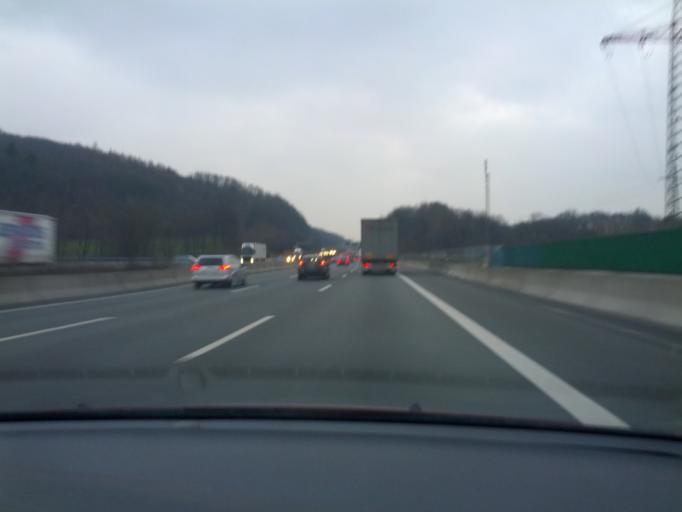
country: DE
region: North Rhine-Westphalia
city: Schwerte
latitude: 51.4170
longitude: 7.5109
